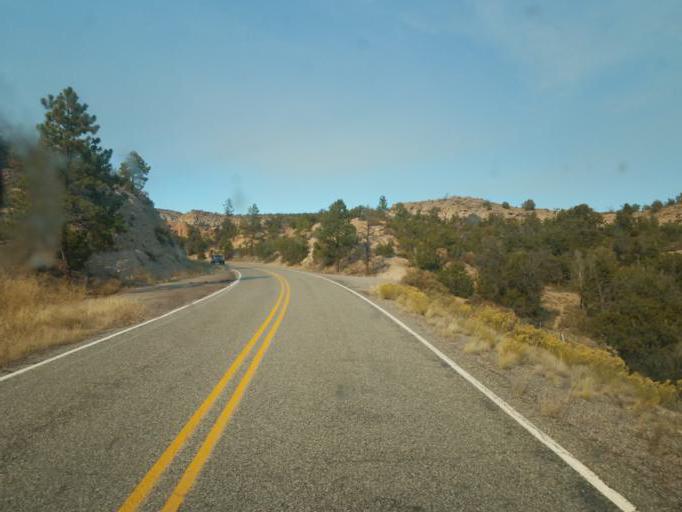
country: US
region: New Mexico
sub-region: Los Alamos County
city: White Rock
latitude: 35.8017
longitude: -106.2453
